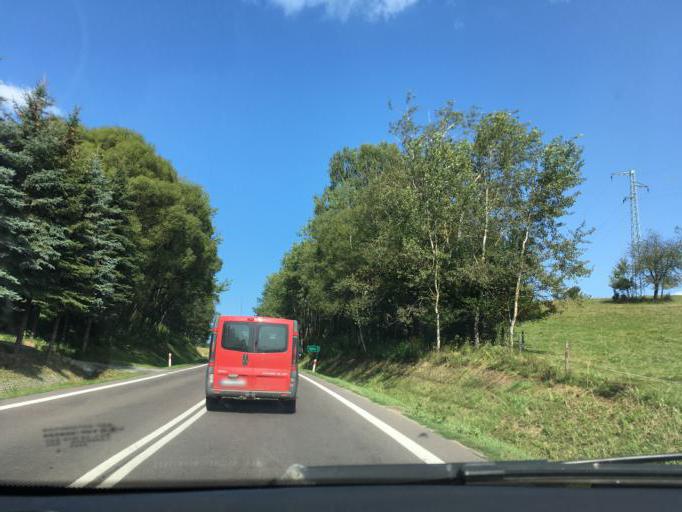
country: PL
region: Subcarpathian Voivodeship
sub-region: Powiat leski
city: Lesko
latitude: 49.4978
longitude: 22.3054
